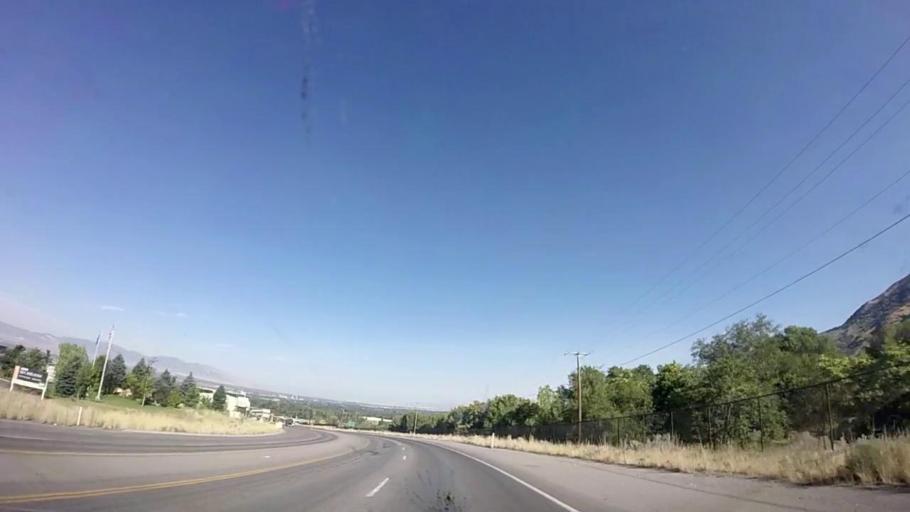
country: US
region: Utah
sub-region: Salt Lake County
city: Cottonwood Heights
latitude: 40.6346
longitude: -111.8008
